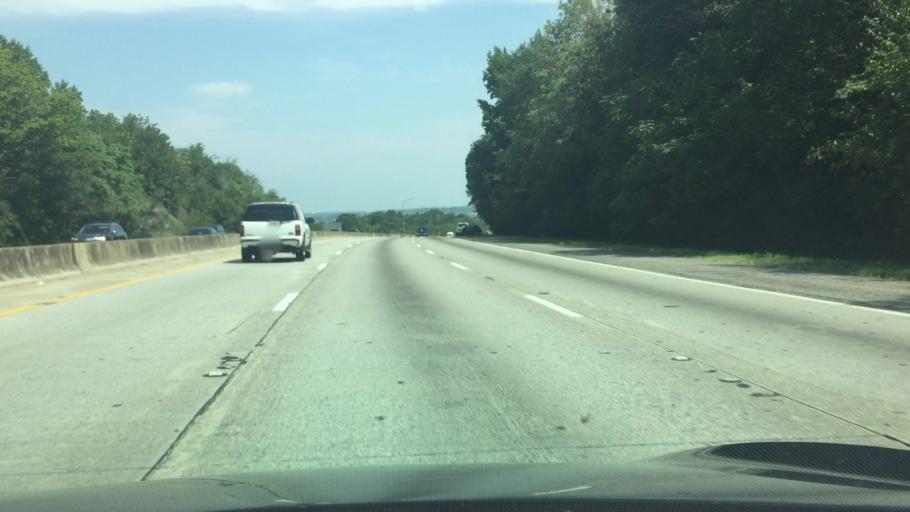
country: US
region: Alabama
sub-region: Jefferson County
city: Homewood
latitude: 33.4730
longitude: -86.8287
